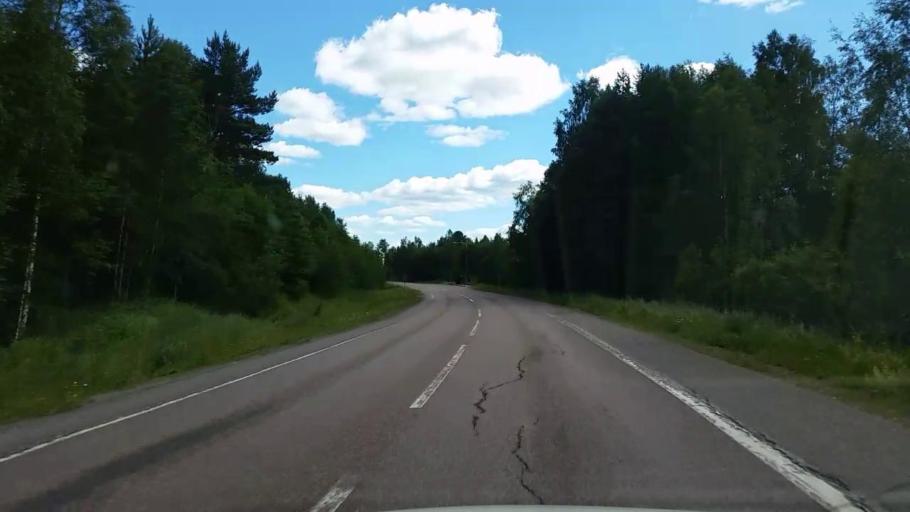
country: SE
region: Dalarna
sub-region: Faluns Kommun
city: Svardsjo
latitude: 60.8508
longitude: 15.7528
